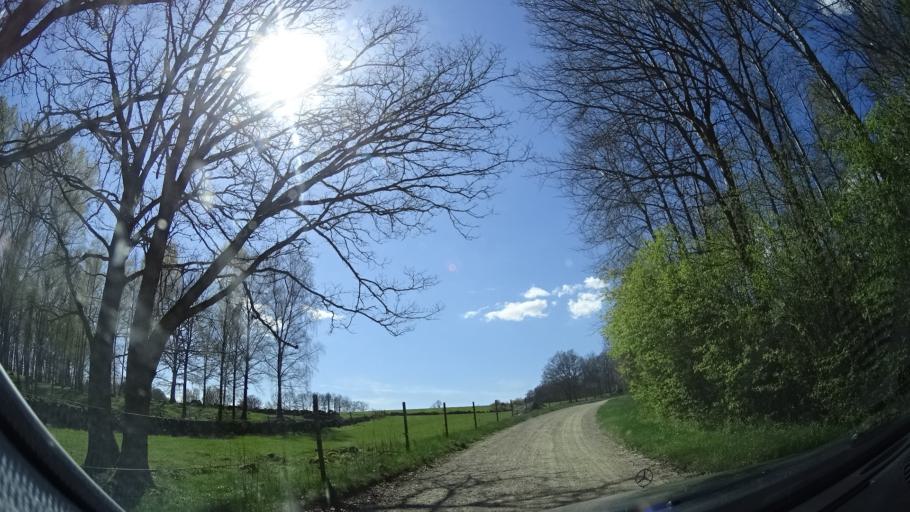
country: SE
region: Skane
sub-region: Hassleholms Kommun
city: Tormestorp
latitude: 56.0857
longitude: 13.7018
